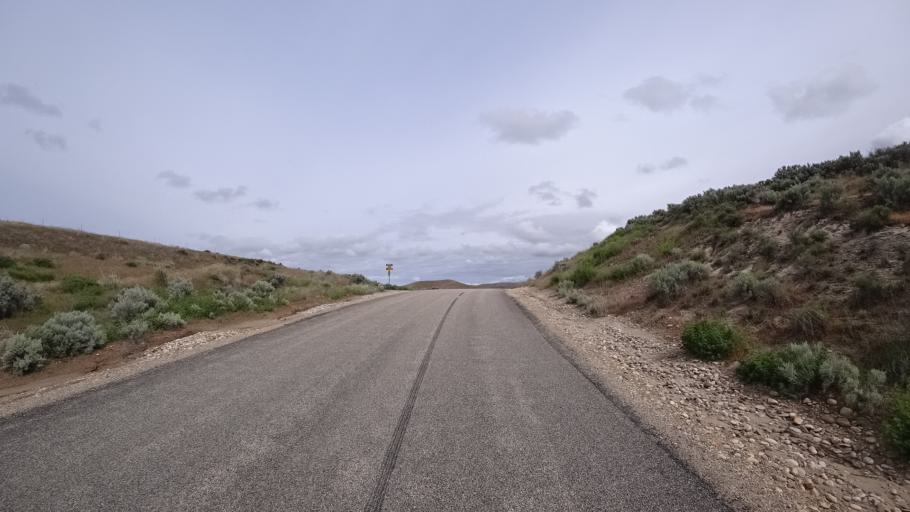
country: US
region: Idaho
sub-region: Ada County
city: Eagle
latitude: 43.7592
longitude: -116.3688
